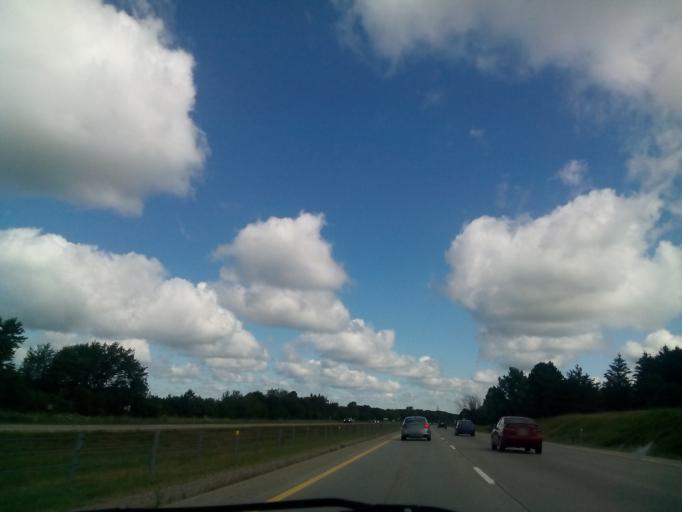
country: US
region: Michigan
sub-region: Genesee County
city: Linden
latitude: 42.7415
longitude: -83.7640
